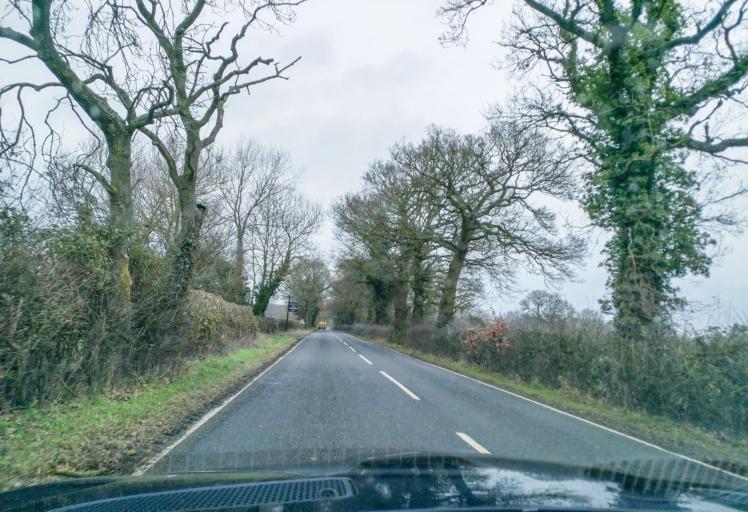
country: GB
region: England
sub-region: Warwickshire
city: Wroxall
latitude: 52.3215
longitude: -1.6707
